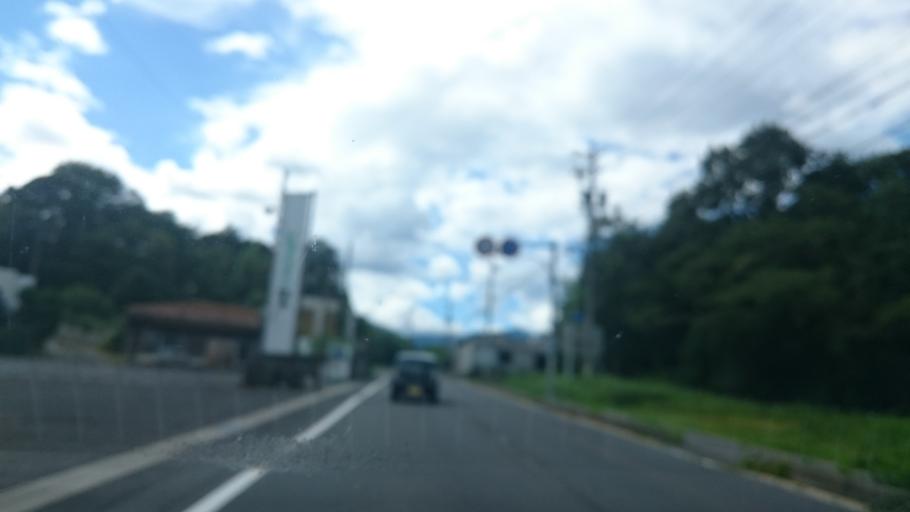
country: JP
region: Gifu
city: Nakatsugawa
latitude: 35.5301
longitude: 137.4614
